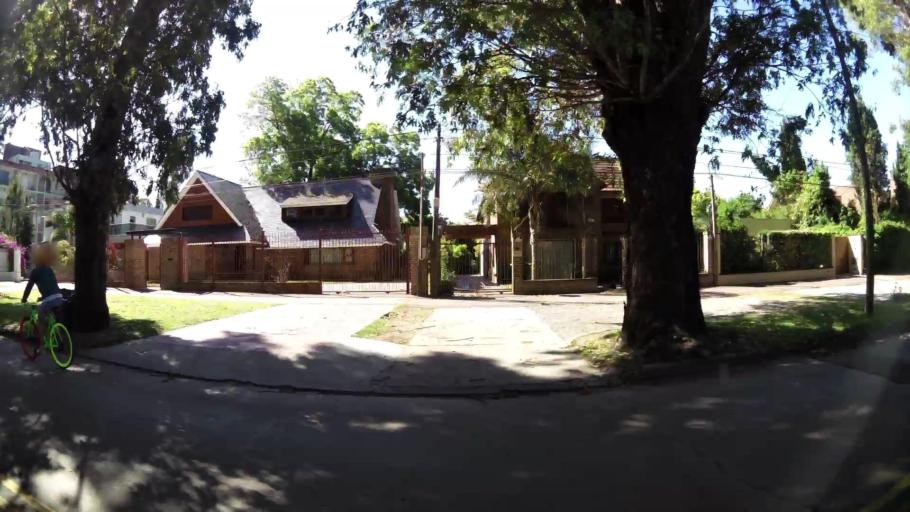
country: UY
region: Canelones
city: Paso de Carrasco
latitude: -34.8903
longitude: -56.0703
